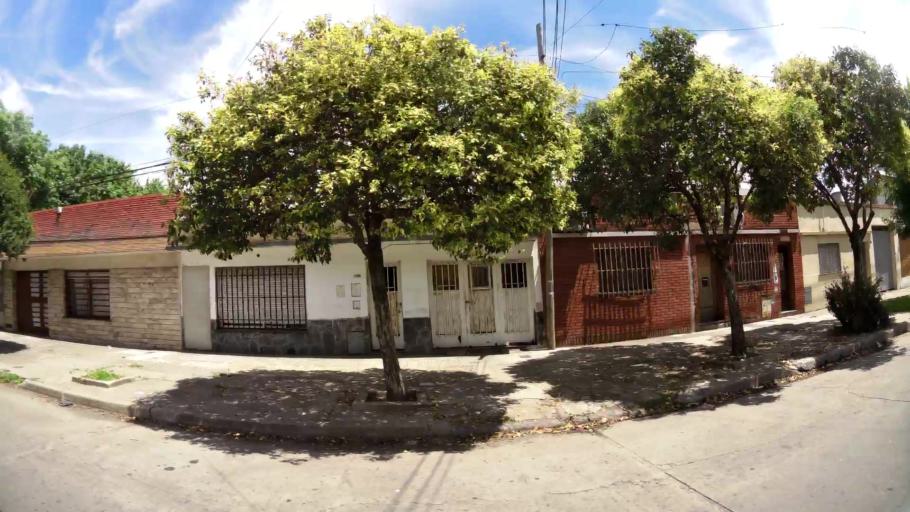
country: AR
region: Santa Fe
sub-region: Departamento de Rosario
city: Rosario
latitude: -32.9793
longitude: -60.6304
